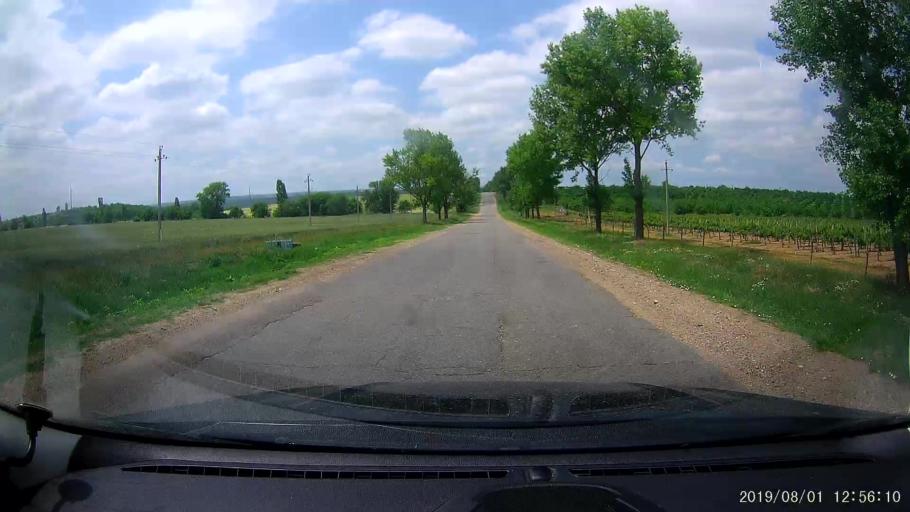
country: MD
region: Gagauzia
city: Vulcanesti
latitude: 45.6924
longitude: 28.4521
